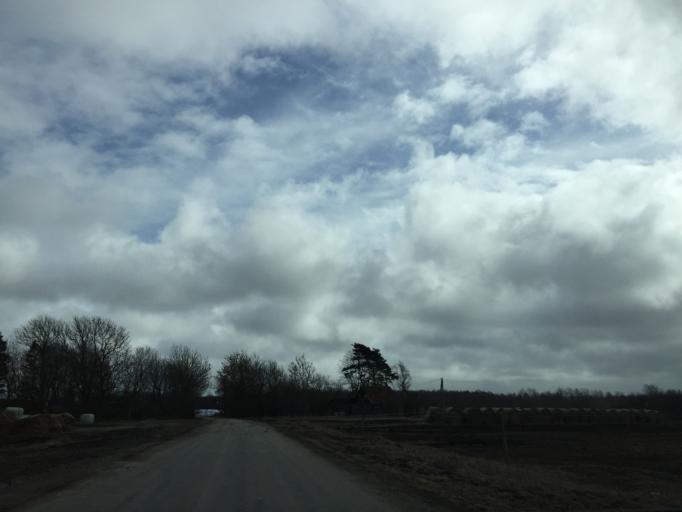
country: EE
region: Laeaene
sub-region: Lihula vald
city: Lihula
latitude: 58.7340
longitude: 23.8616
